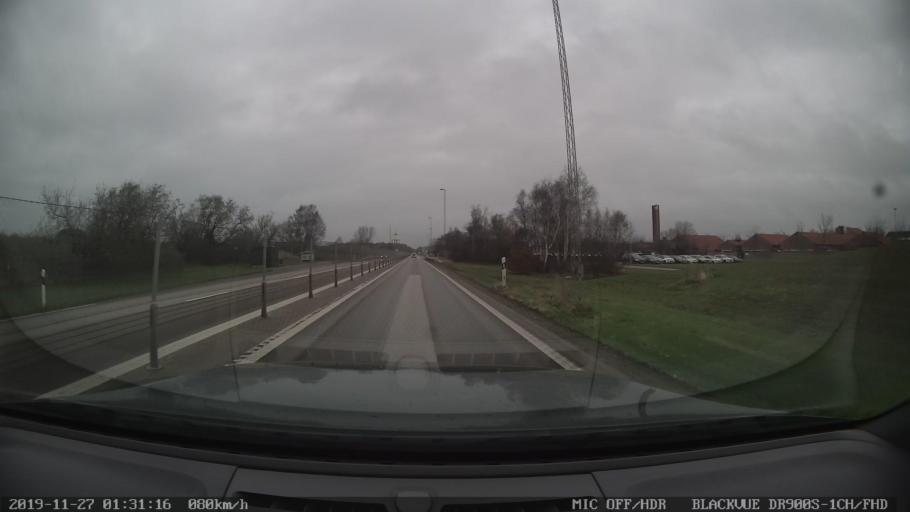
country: SE
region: Skane
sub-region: Hoganas Kommun
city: Hoganas
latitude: 56.1753
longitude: 12.5634
